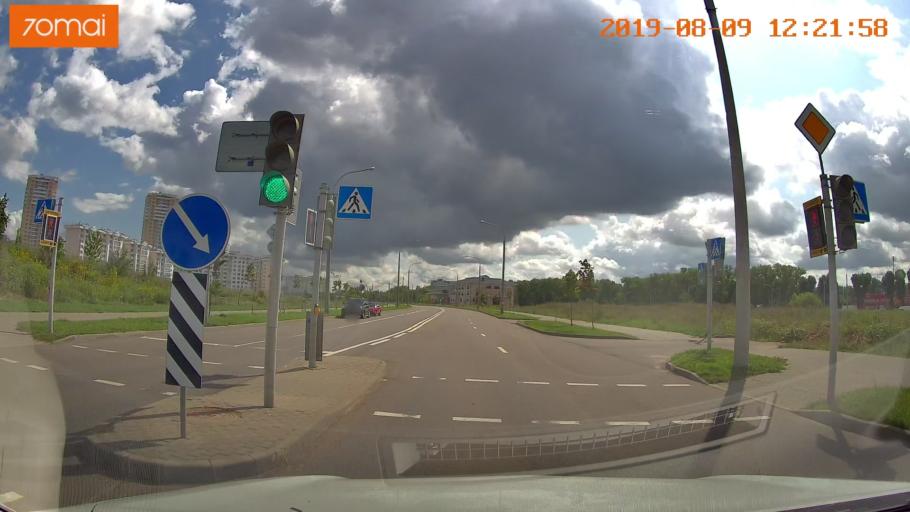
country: BY
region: Minsk
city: Zhdanovichy
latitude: 53.9338
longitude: 27.4652
